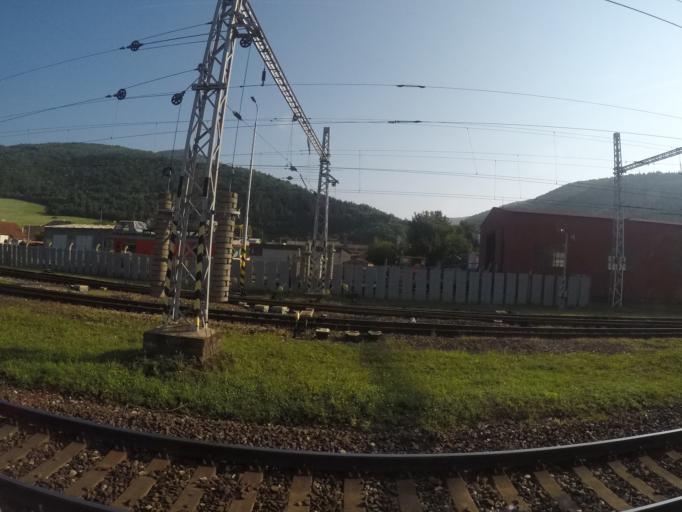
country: SK
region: Kosicky
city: Gelnica
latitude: 48.8944
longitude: 21.0146
